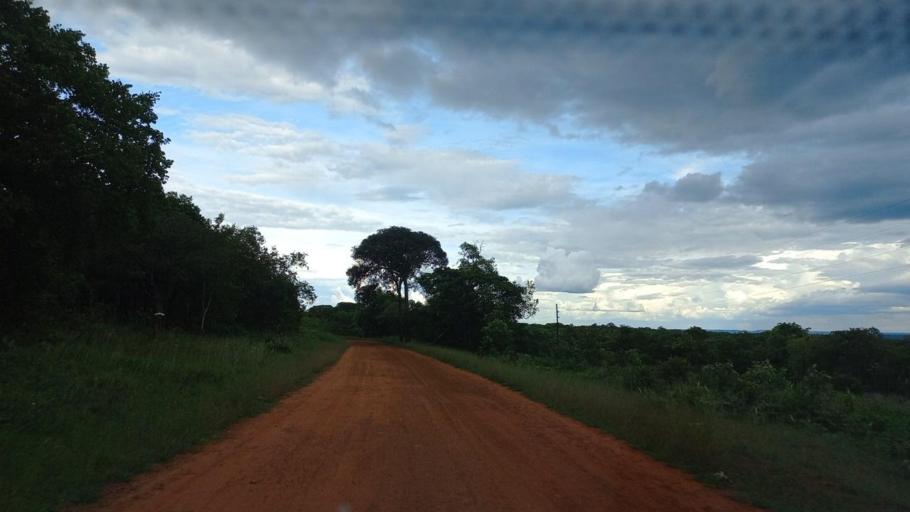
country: ZM
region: North-Western
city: Mwinilunga
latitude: -11.7781
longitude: 24.3825
